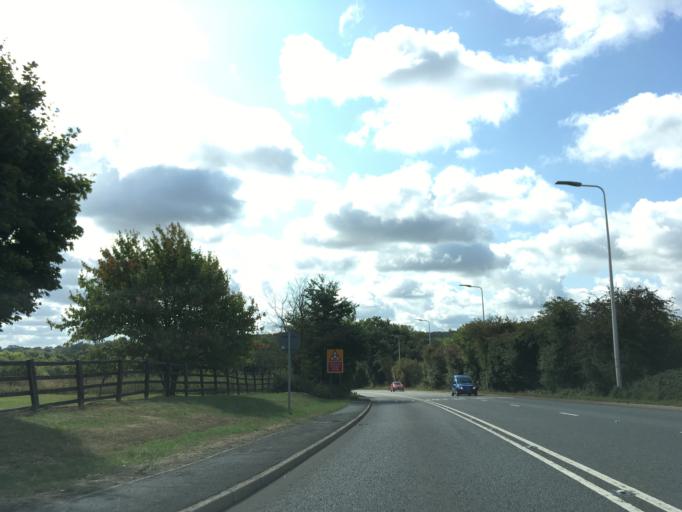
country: GB
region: England
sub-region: West Berkshire
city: Greenham
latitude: 51.3762
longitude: -1.3188
